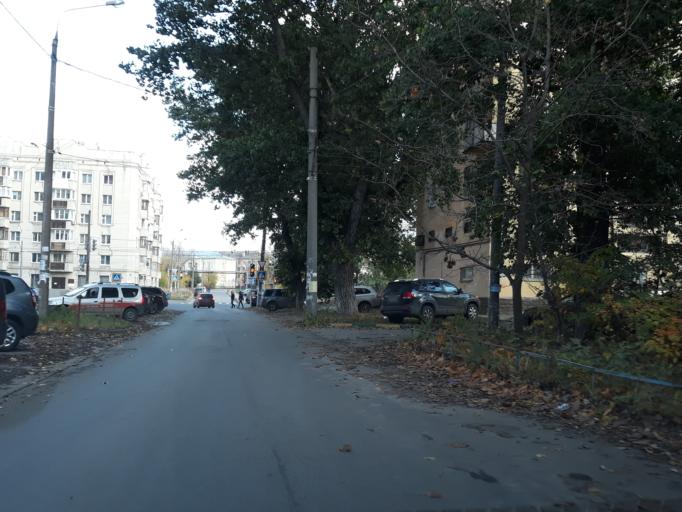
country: RU
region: Nizjnij Novgorod
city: Nizhniy Novgorod
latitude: 56.3032
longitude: 43.9370
